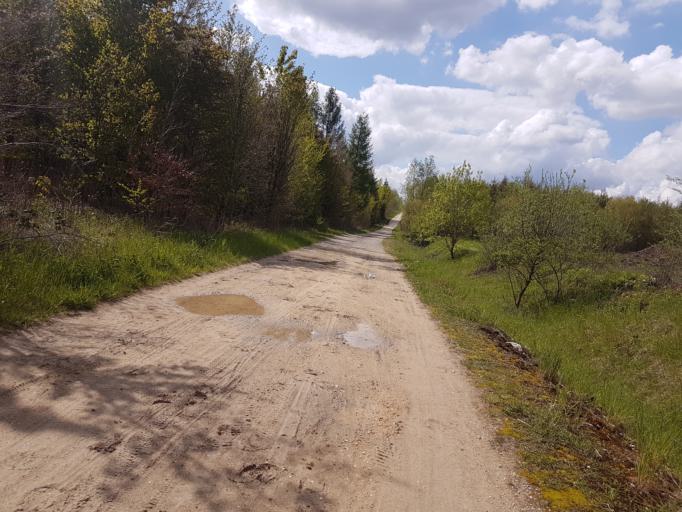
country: CH
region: Solothurn
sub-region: Bezirk Olten
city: Gunzgen
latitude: 47.2994
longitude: 7.8455
